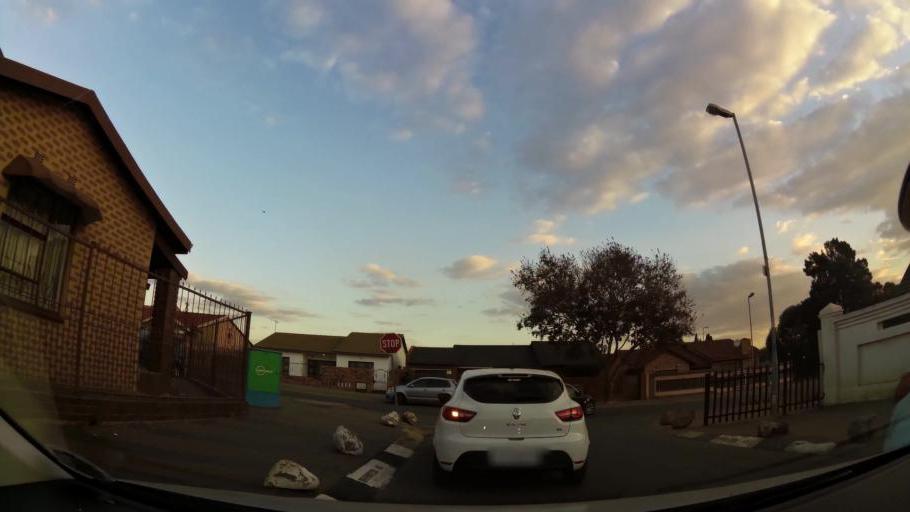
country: ZA
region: Gauteng
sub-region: City of Johannesburg Metropolitan Municipality
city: Soweto
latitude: -26.2732
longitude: 27.8974
